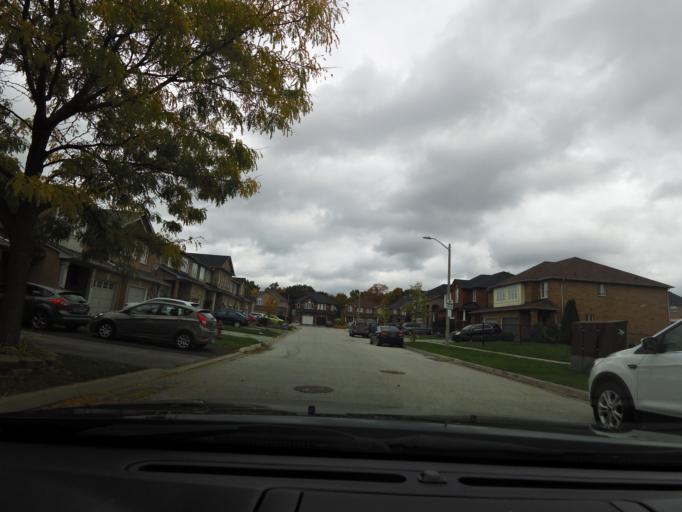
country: CA
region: Ontario
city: Burlington
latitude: 43.3929
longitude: -79.7787
